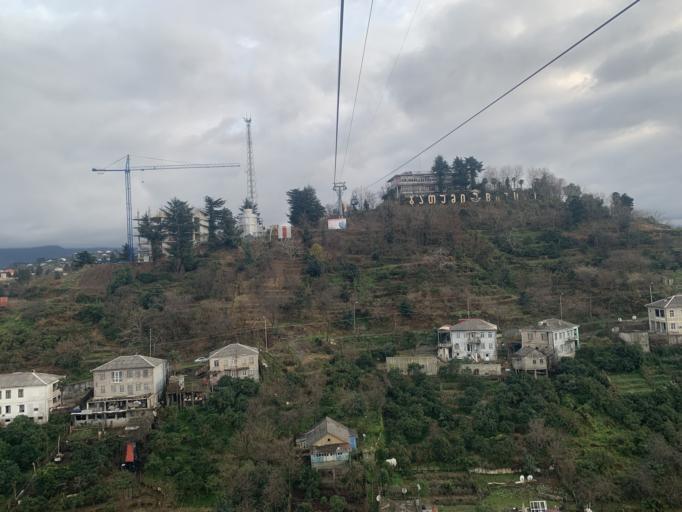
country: GE
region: Ajaria
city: Batumi
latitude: 41.6385
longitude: 41.6500
